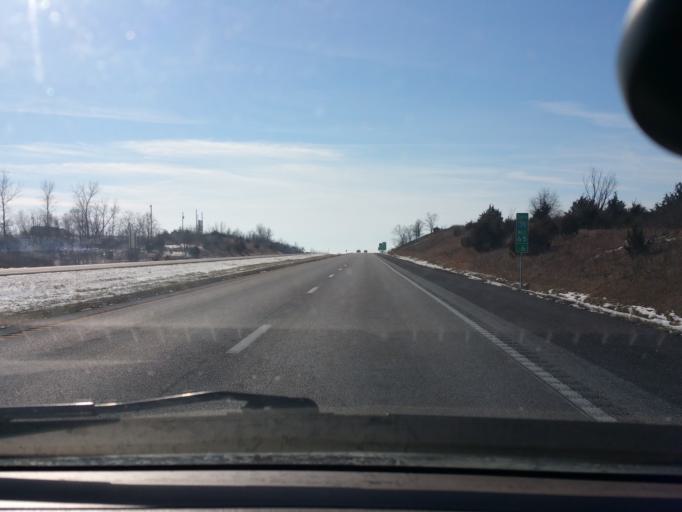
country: US
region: Missouri
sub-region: Daviess County
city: Gallatin
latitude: 39.9086
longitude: -94.1469
